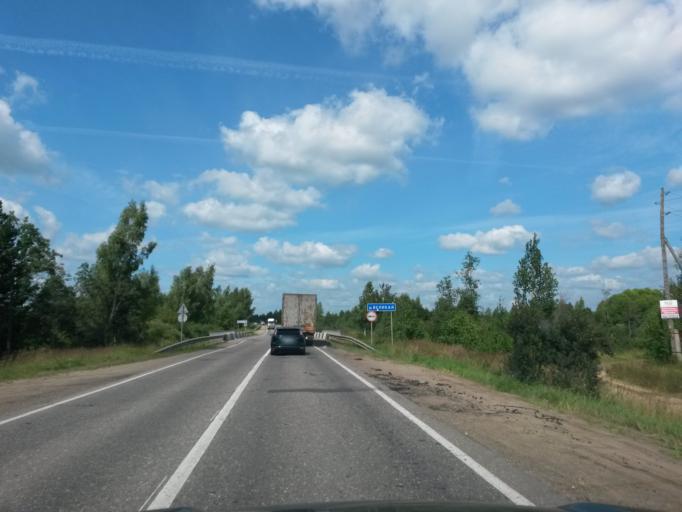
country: RU
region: Jaroslavl
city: Yaroslavl
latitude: 57.5100
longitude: 39.8976
